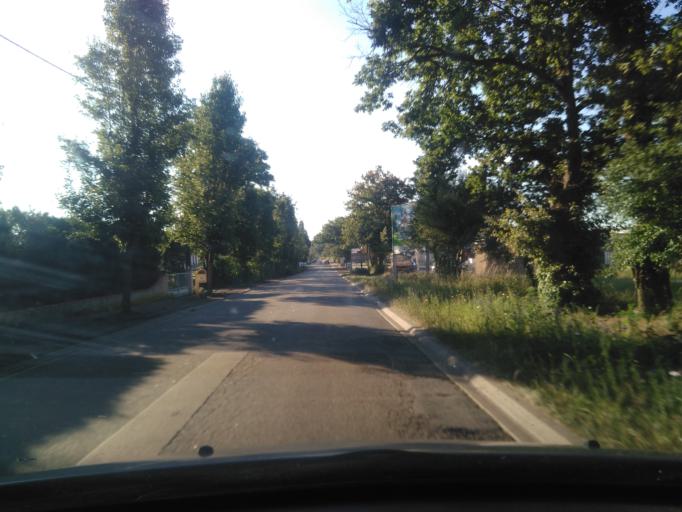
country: FR
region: Pays de la Loire
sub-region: Departement de la Vendee
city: Dompierre-sur-Yon
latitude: 46.7383
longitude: -1.4002
